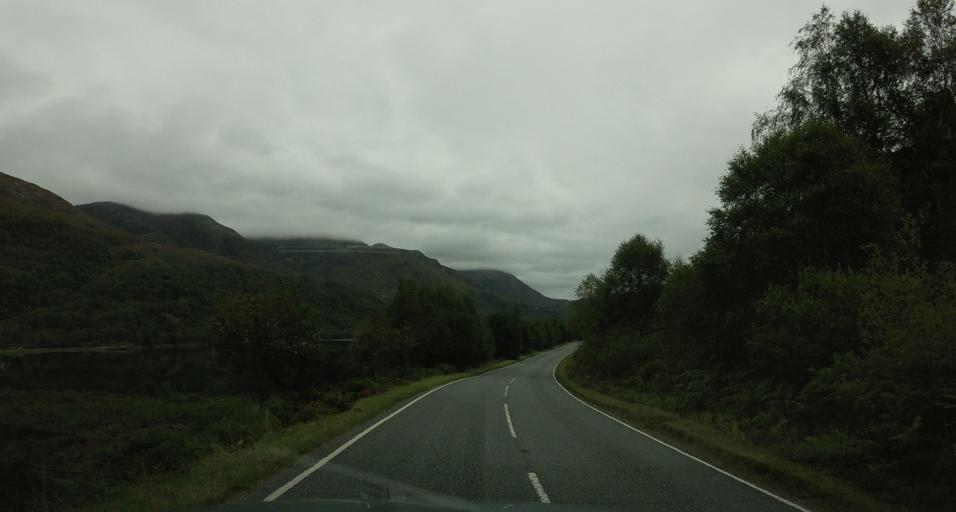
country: GB
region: Scotland
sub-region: Highland
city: Fort William
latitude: 56.7055
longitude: -5.0245
